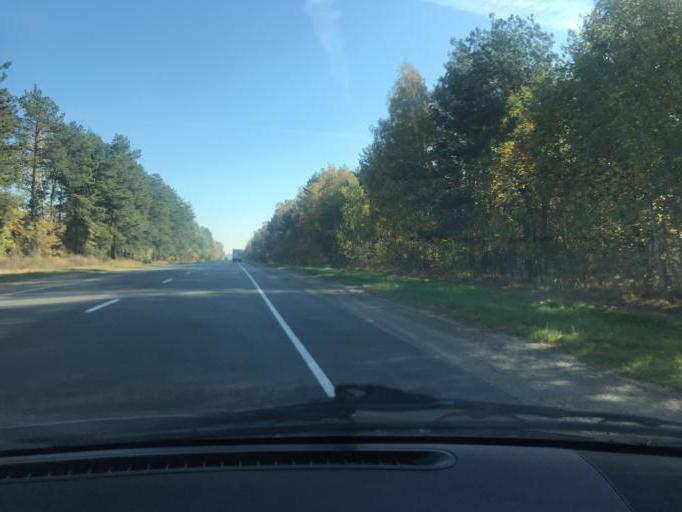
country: BY
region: Brest
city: Ivanava
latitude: 52.1545
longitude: 25.5904
